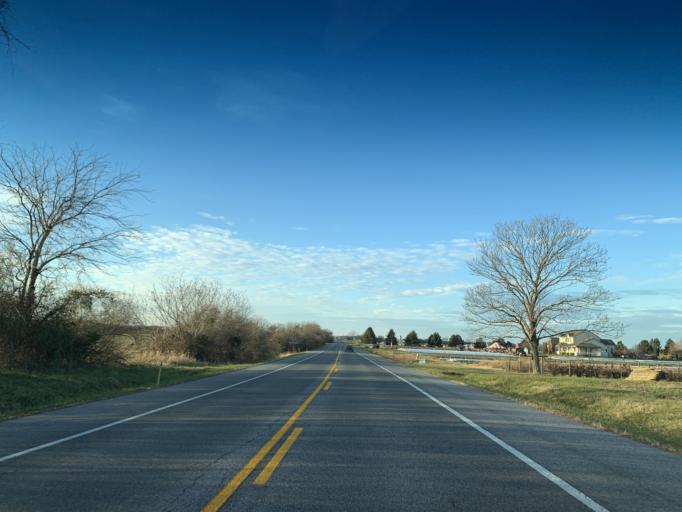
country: US
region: Maryland
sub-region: Kent County
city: Chestertown
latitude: 39.2524
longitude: -76.0775
